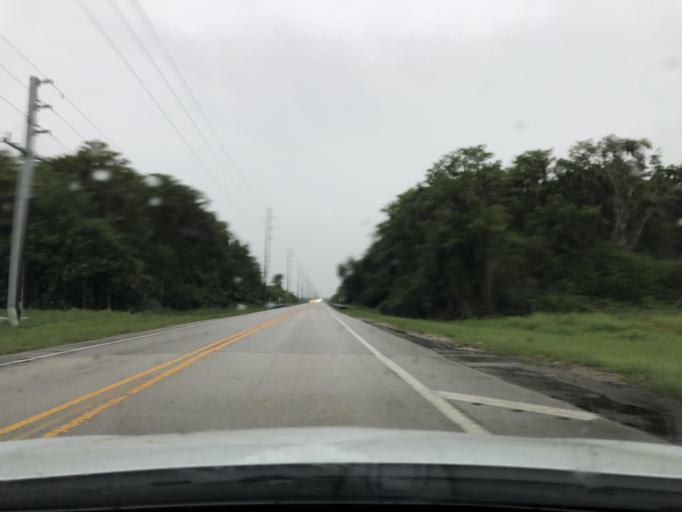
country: US
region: Florida
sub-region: Collier County
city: Orangetree
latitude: 26.2938
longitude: -81.4900
